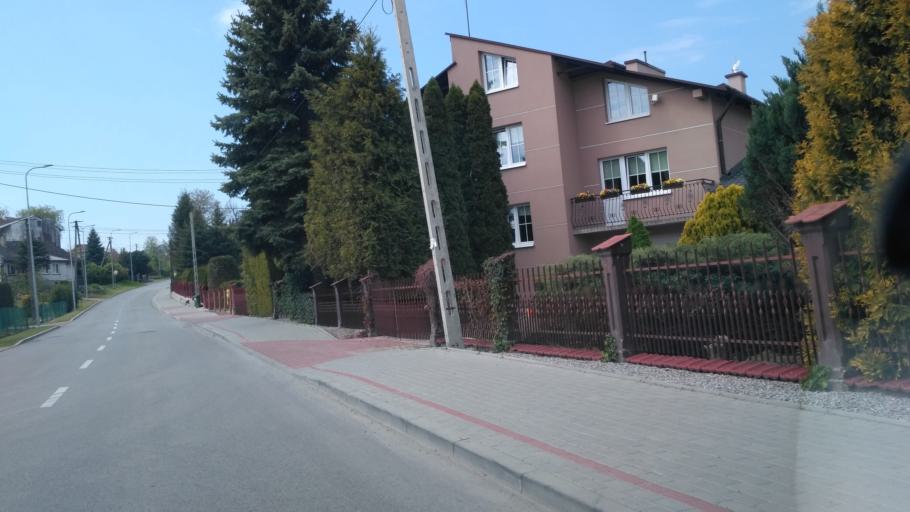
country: PL
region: Subcarpathian Voivodeship
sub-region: Powiat jaroslawski
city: Jaroslaw
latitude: 50.0119
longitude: 22.6627
